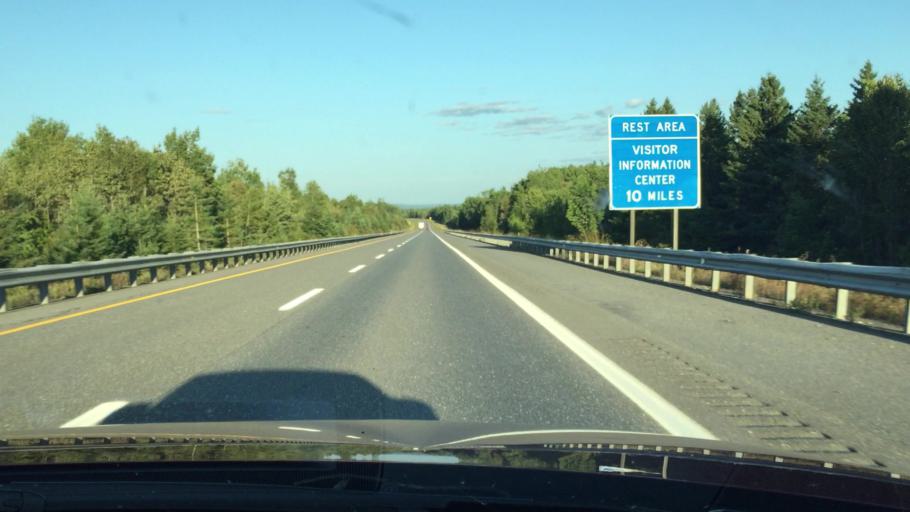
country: US
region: Maine
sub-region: Aroostook County
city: Hodgdon
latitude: 46.1427
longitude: -68.0388
